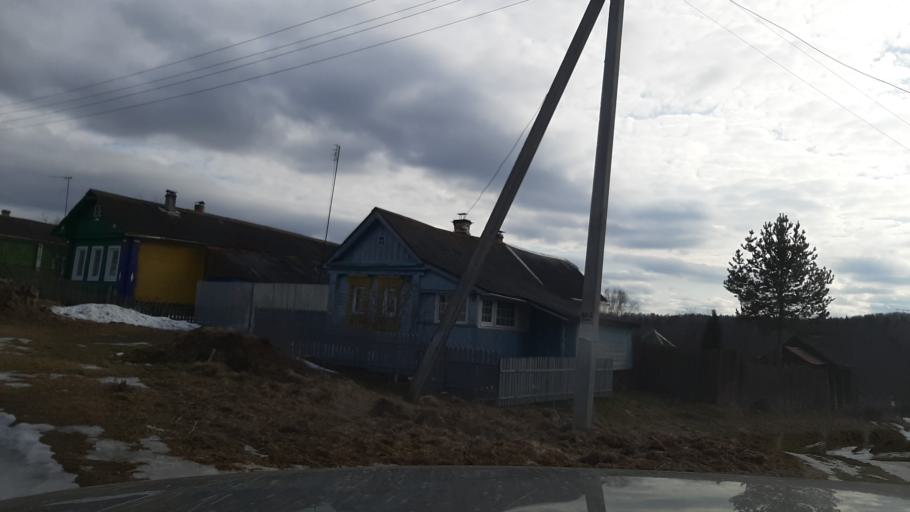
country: RU
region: Ivanovo
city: Teykovo
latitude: 56.8992
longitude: 40.6776
